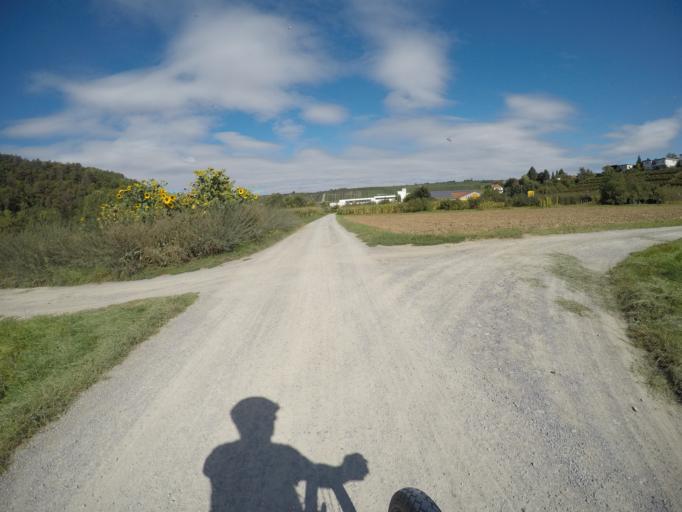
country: DE
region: Baden-Wuerttemberg
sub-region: Regierungsbezirk Stuttgart
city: Mundelsheim
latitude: 48.9919
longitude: 9.2055
